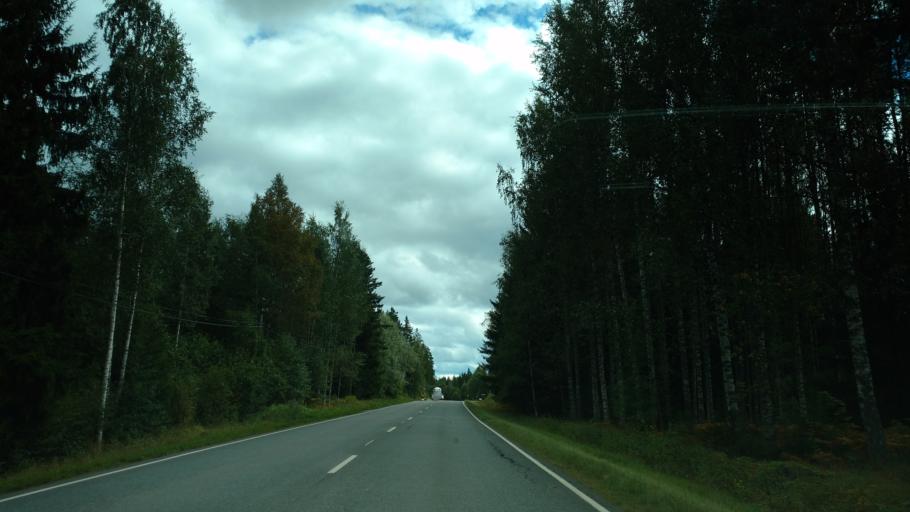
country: FI
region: Haeme
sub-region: Forssa
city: Ypaejae
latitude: 60.7996
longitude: 23.2495
